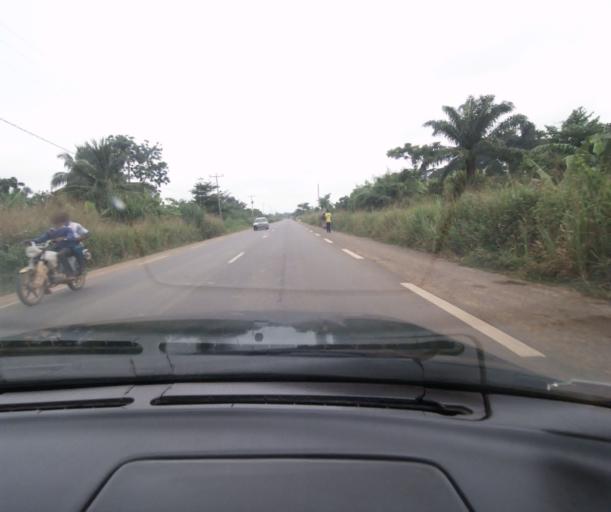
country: CM
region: Centre
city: Saa
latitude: 4.3565
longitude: 11.2772
